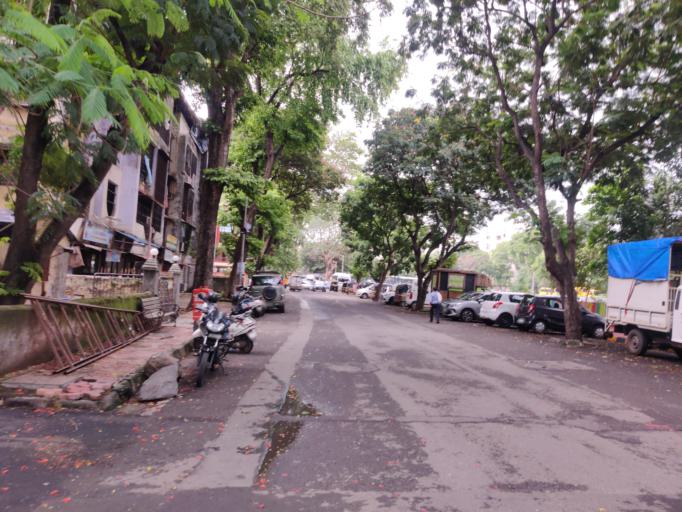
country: IN
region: Maharashtra
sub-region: Mumbai Suburban
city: Borivli
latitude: 19.2535
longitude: 72.8567
